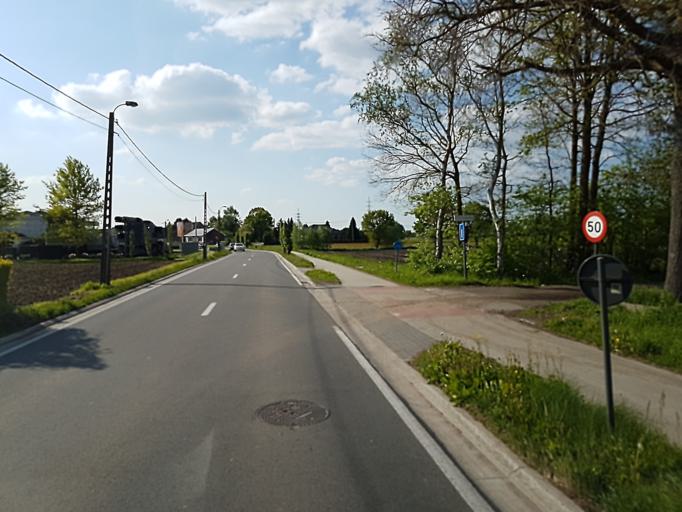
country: BE
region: Flanders
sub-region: Provincie Antwerpen
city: Putte
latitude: 51.0408
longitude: 4.6166
